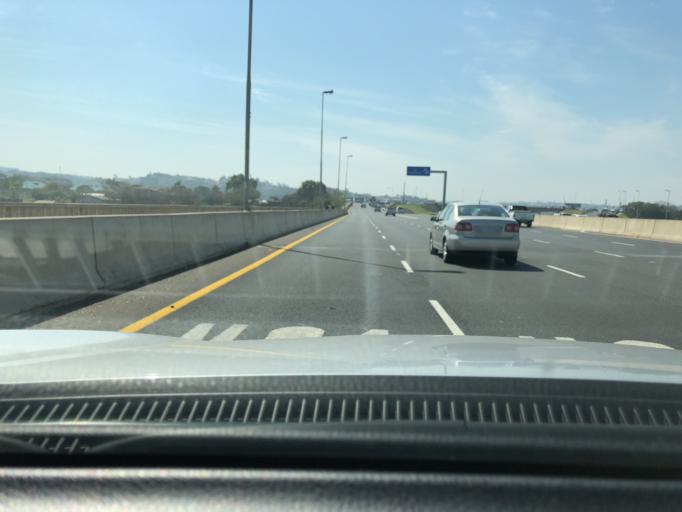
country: ZA
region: KwaZulu-Natal
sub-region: eThekwini Metropolitan Municipality
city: Berea
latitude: -29.8038
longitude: 30.9799
